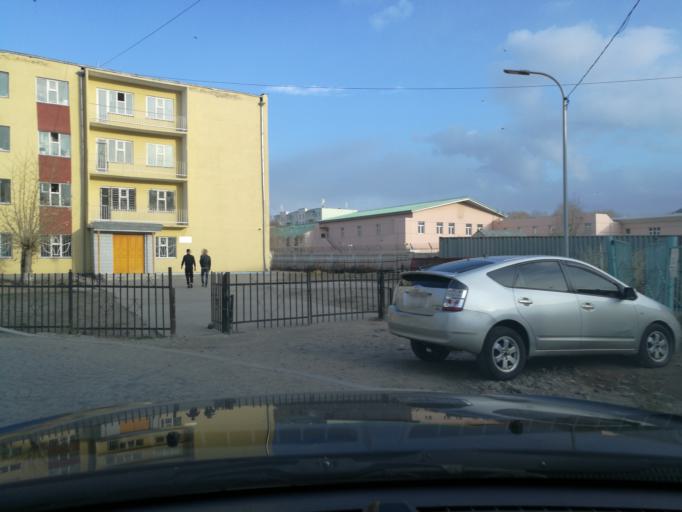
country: MN
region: Ulaanbaatar
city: Ulaanbaatar
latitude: 47.9253
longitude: 106.9226
